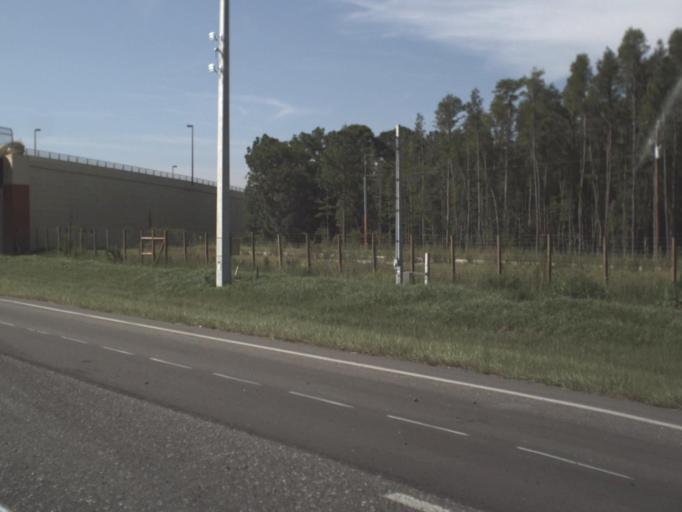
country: US
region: Florida
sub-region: Hillsborough County
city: Pebble Creek
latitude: 28.1439
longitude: -82.3834
